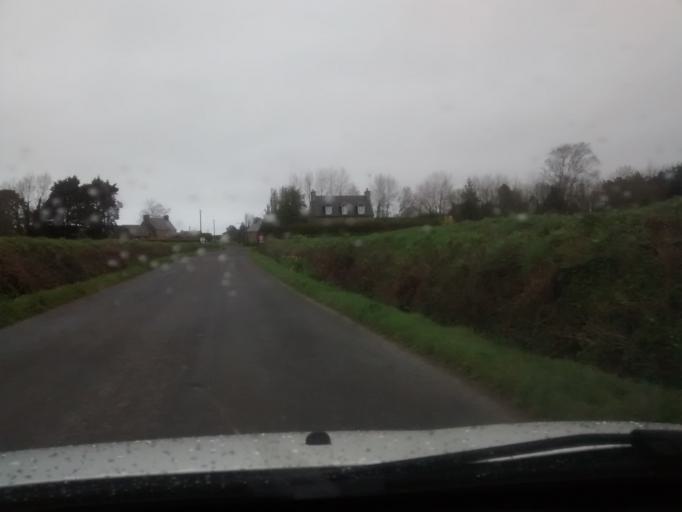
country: FR
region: Brittany
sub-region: Departement des Cotes-d'Armor
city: Penvenan
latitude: 48.8200
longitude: -3.2849
